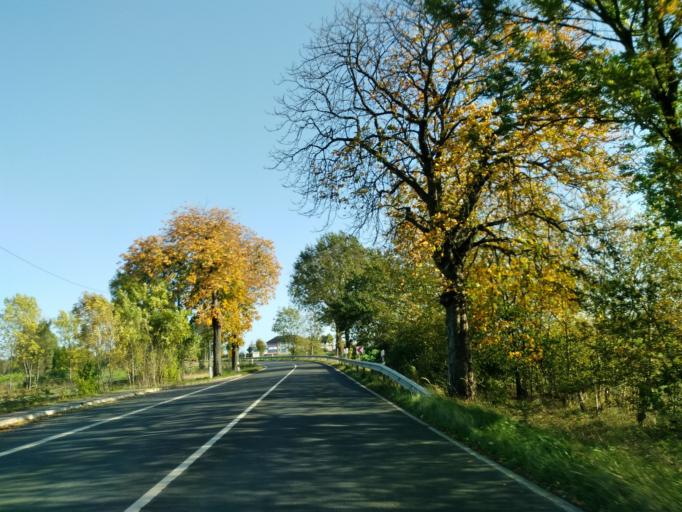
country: DE
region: Rheinland-Pfalz
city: Asbach
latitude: 50.7169
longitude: 7.3961
